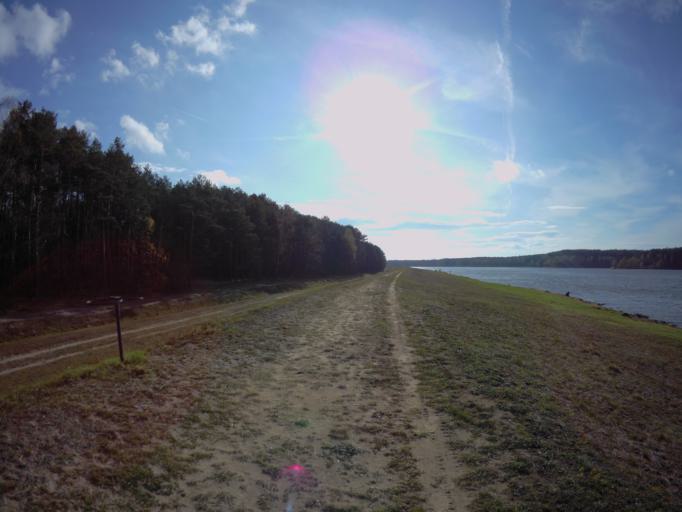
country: PL
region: Subcarpathian Voivodeship
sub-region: Powiat kolbuszowski
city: Lipnica
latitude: 50.3345
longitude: 21.9440
